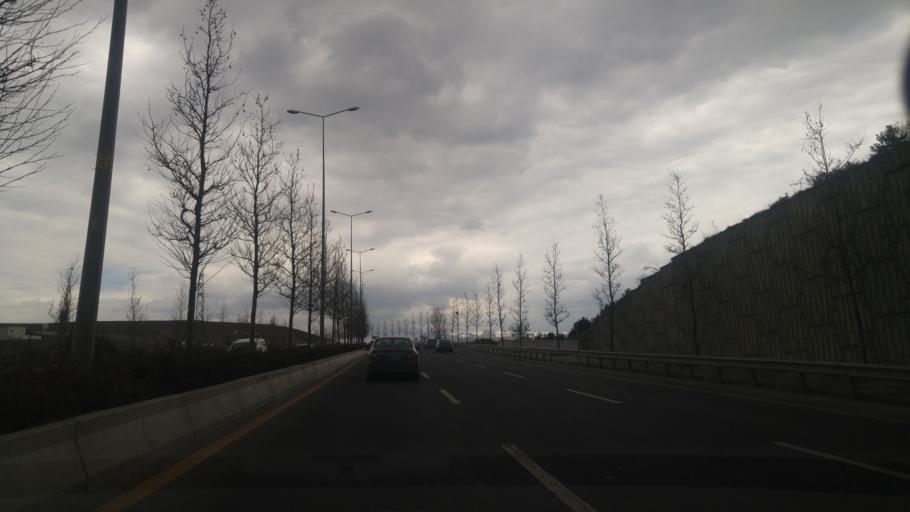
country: TR
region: Ankara
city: Mamak
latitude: 39.8868
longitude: 32.9142
